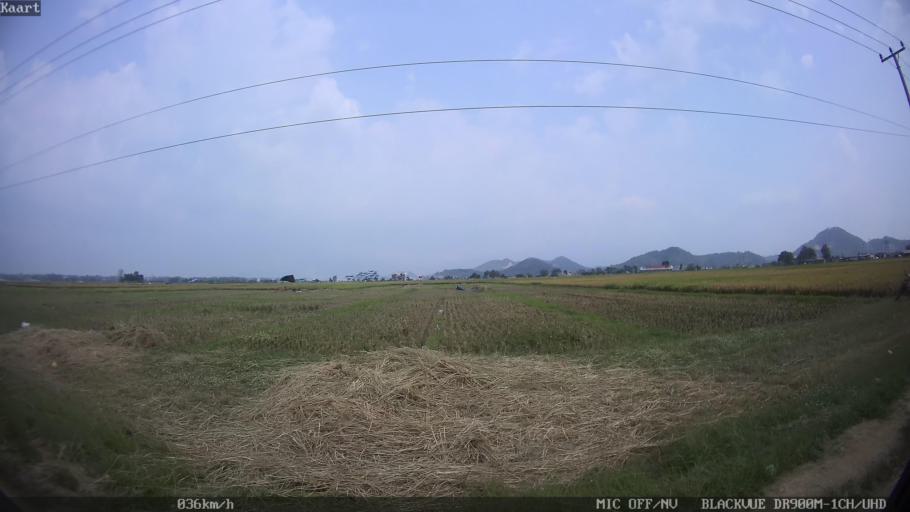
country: ID
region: Lampung
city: Pringsewu
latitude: -5.3622
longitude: 105.0058
